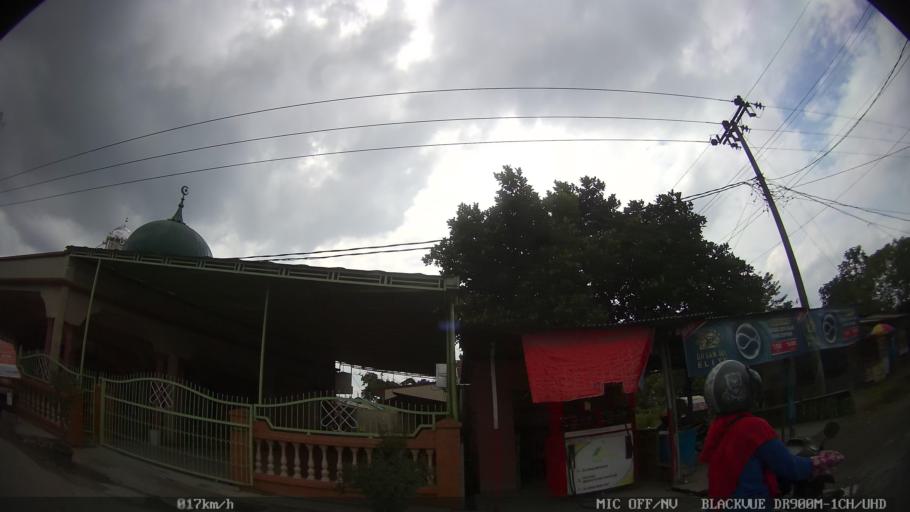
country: ID
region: North Sumatra
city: Sunggal
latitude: 3.6194
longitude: 98.6052
